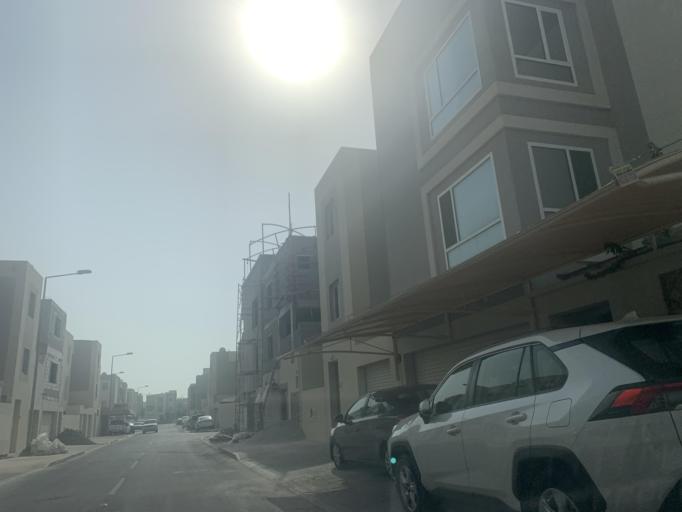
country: BH
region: Manama
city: Jidd Hafs
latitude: 26.2329
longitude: 50.4520
